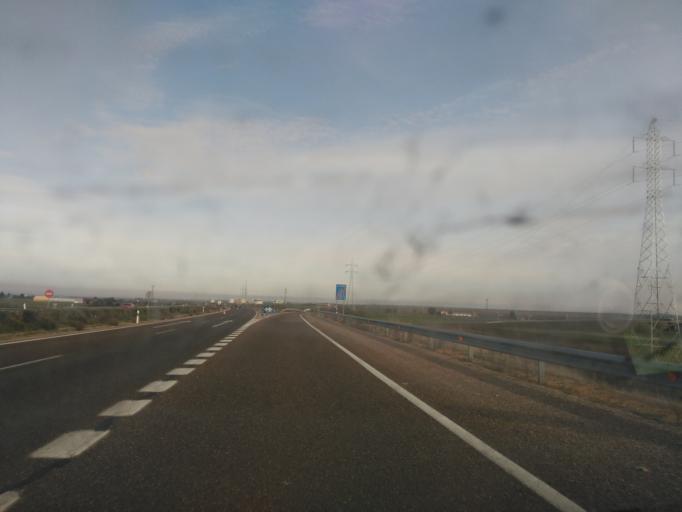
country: ES
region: Castille and Leon
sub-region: Provincia de Salamanca
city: Castellanos de Moriscos
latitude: 41.0114
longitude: -5.5897
